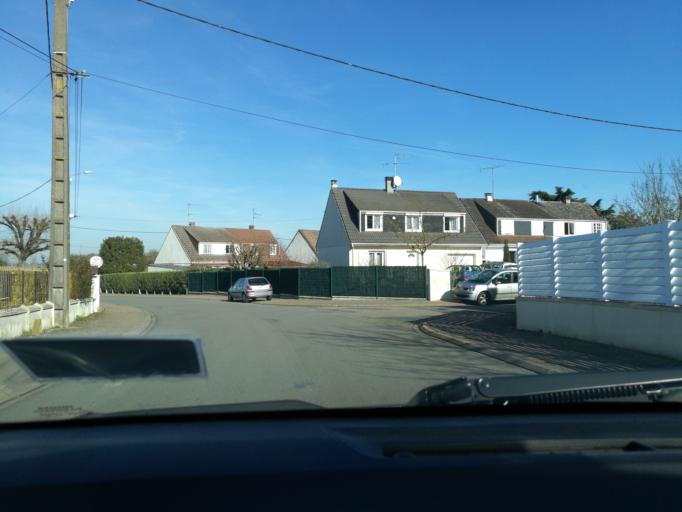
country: FR
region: Centre
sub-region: Departement du Loiret
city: Saint-Ay
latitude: 47.8677
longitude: 1.7652
